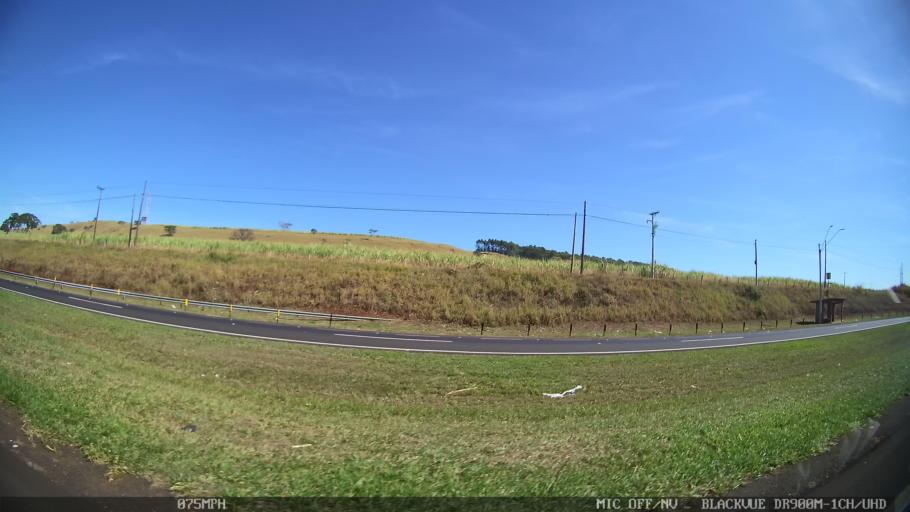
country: BR
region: Sao Paulo
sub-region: Sao Simao
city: Sao Simao
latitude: -21.4635
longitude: -47.6426
